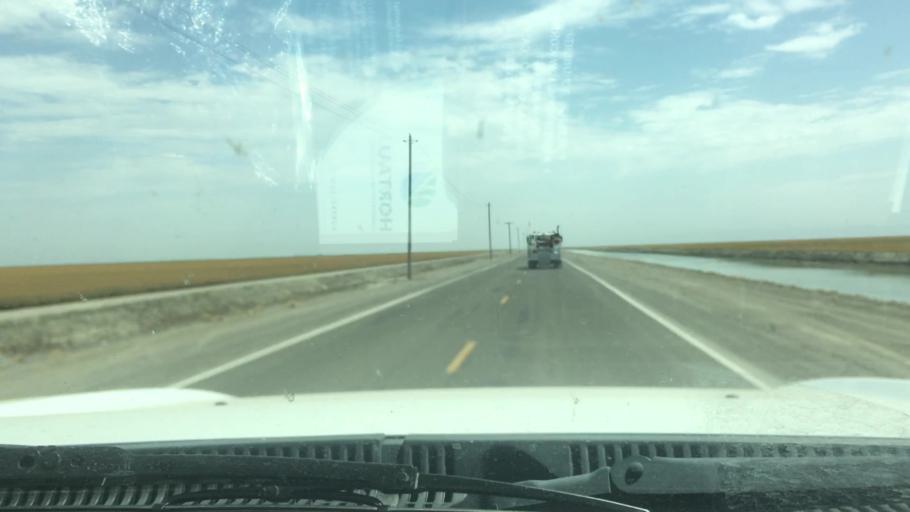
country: US
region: California
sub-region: Tulare County
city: Alpaugh
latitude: 35.9261
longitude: -119.5732
